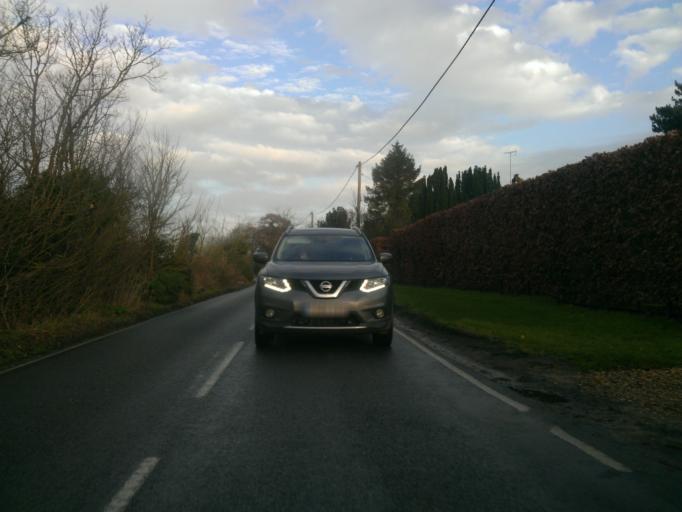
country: GB
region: England
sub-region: Essex
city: Wivenhoe
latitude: 51.8568
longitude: 0.9766
